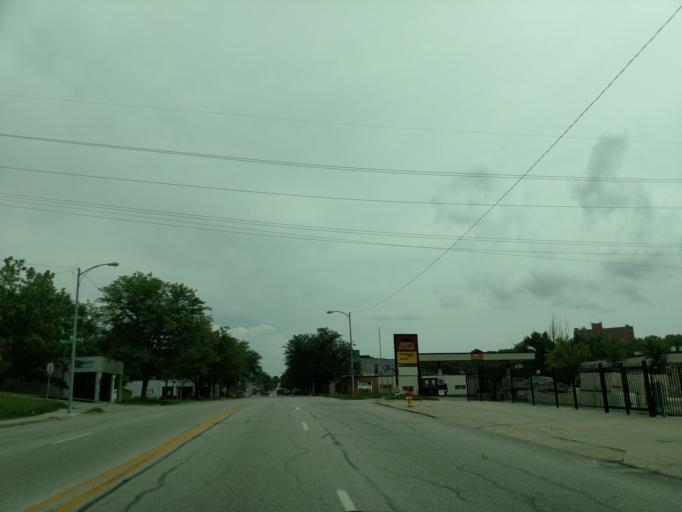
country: US
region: Nebraska
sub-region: Douglas County
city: Omaha
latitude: 41.2486
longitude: -95.9334
